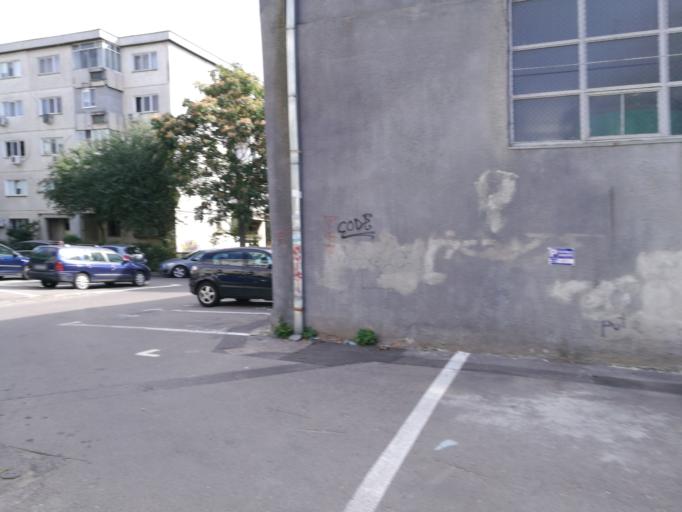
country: RO
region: Bucuresti
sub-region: Municipiul Bucuresti
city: Bucharest
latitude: 44.4806
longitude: 26.0951
